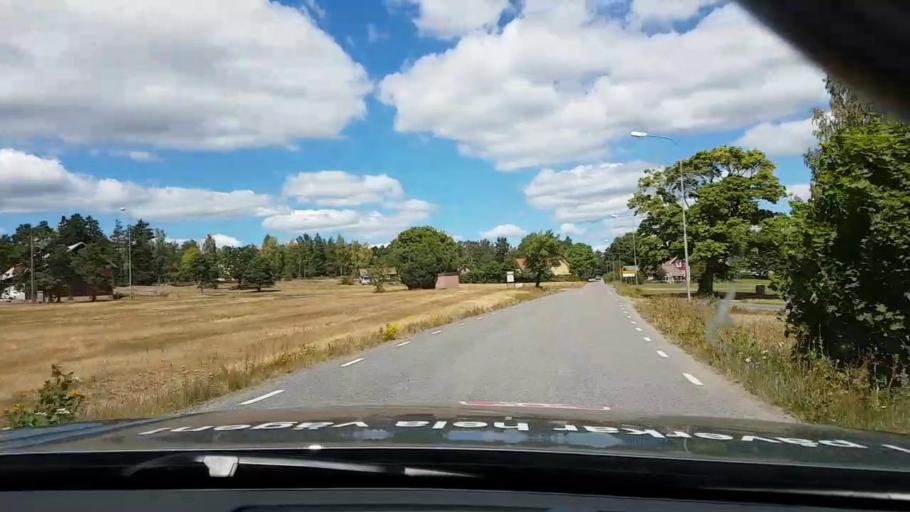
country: SE
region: Kalmar
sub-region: Vasterviks Kommun
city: Forserum
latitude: 58.0090
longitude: 16.5785
